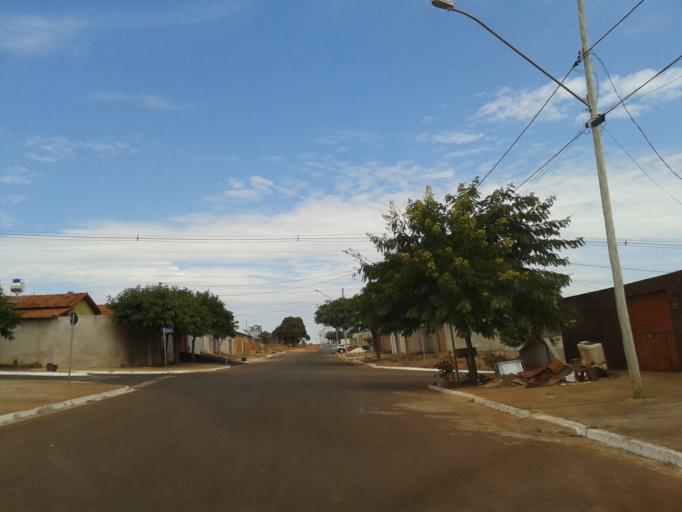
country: BR
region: Minas Gerais
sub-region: Santa Vitoria
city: Santa Vitoria
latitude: -18.8490
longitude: -50.1351
